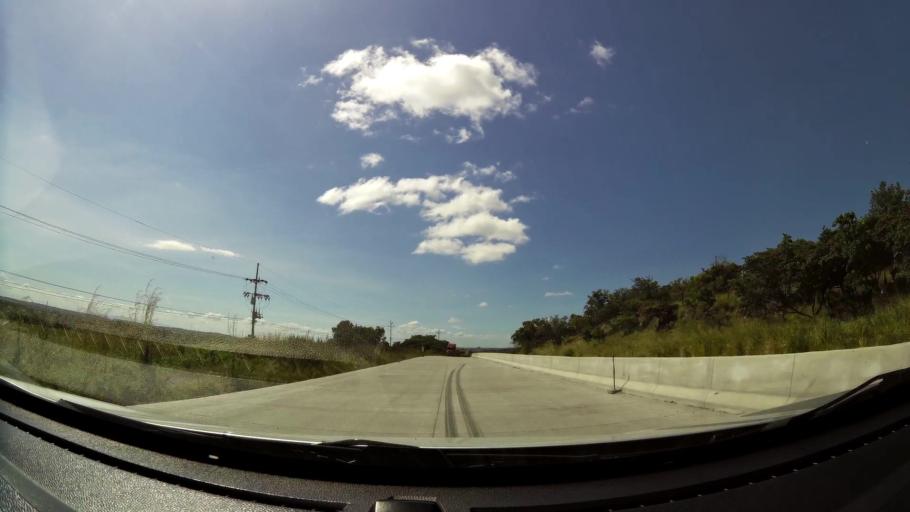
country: CR
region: Guanacaste
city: Bagaces
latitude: 10.5383
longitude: -85.3287
